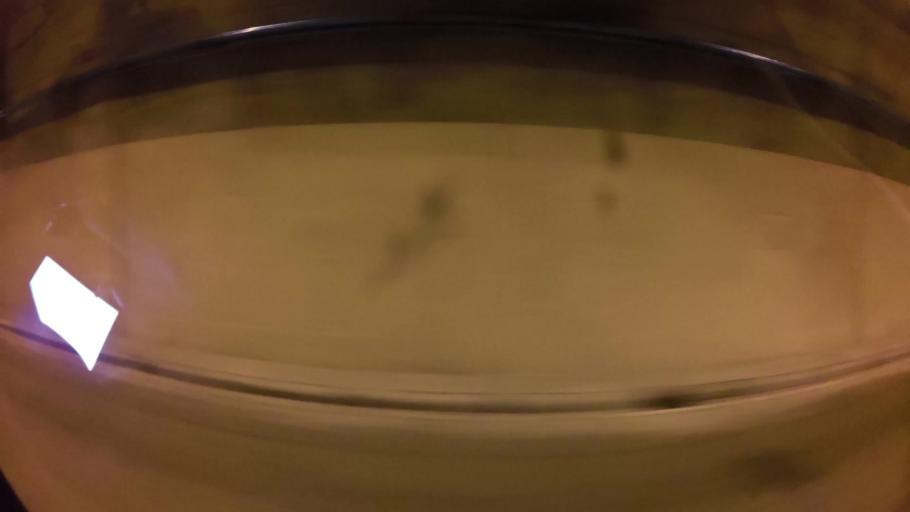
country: EC
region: Guayas
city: Guayaquil
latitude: -2.1732
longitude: -79.9263
